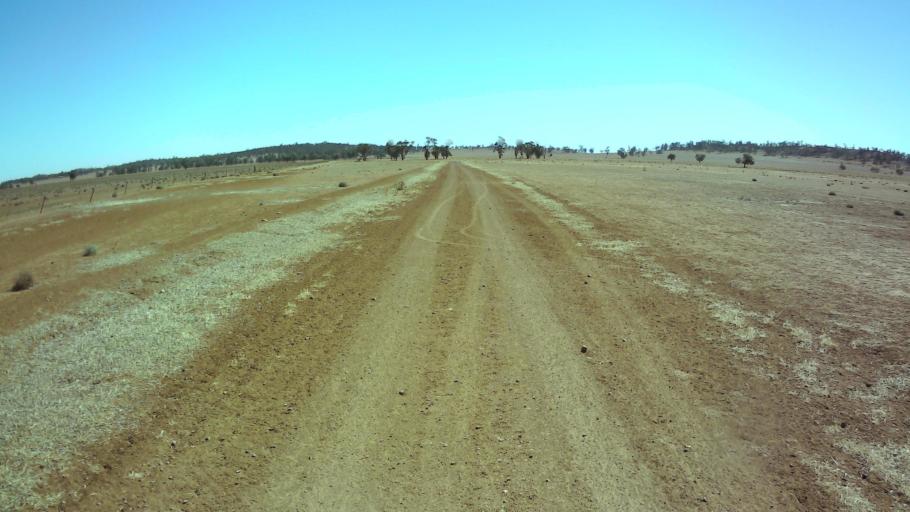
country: AU
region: New South Wales
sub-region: Forbes
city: Forbes
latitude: -33.7029
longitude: 147.6689
